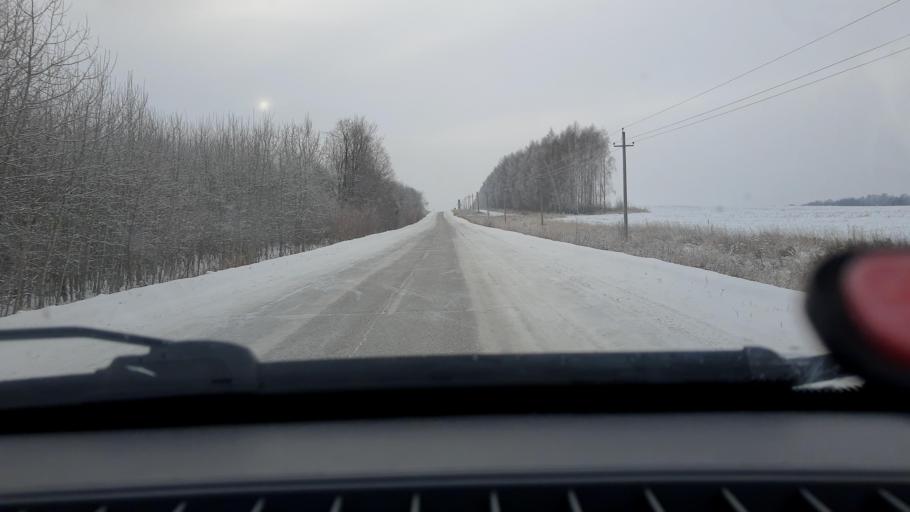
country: RU
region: Bashkortostan
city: Iglino
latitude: 54.6645
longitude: 56.4222
